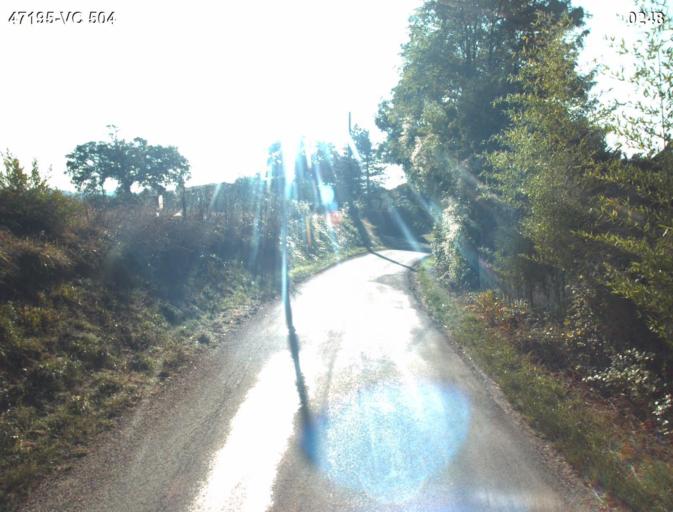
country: FR
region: Aquitaine
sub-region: Departement du Lot-et-Garonne
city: Nerac
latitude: 44.1502
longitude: 0.3361
